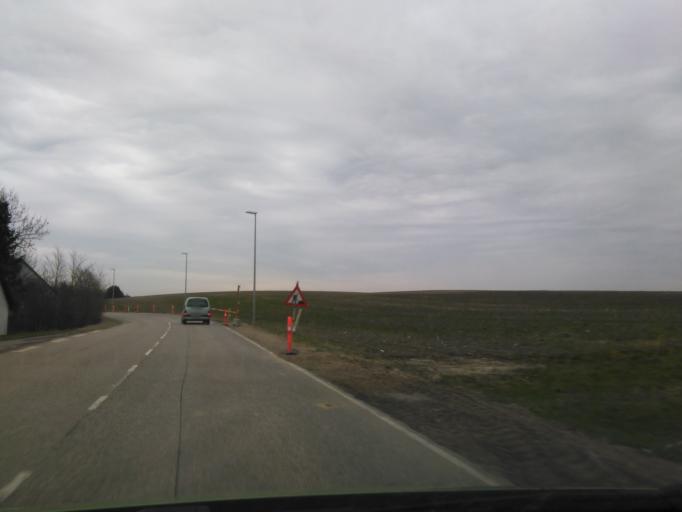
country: DK
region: Central Jutland
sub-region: Randers Kommune
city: Spentrup
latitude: 56.5554
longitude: 10.0014
